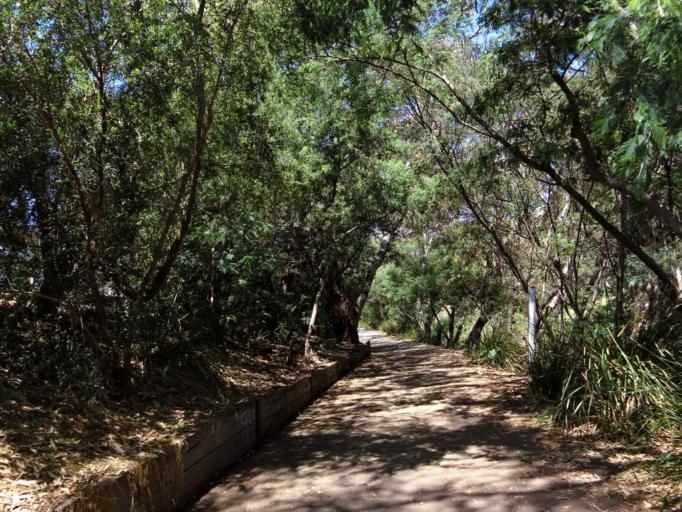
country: AU
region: Victoria
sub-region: Moreland
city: Coburg
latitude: -37.7469
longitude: 144.9807
